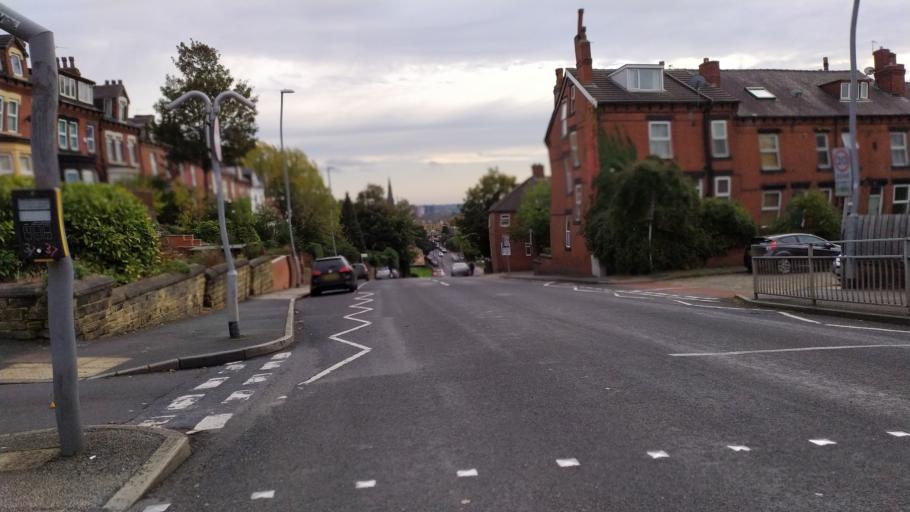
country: GB
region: England
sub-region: City and Borough of Leeds
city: Leeds
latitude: 53.8104
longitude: -1.5849
